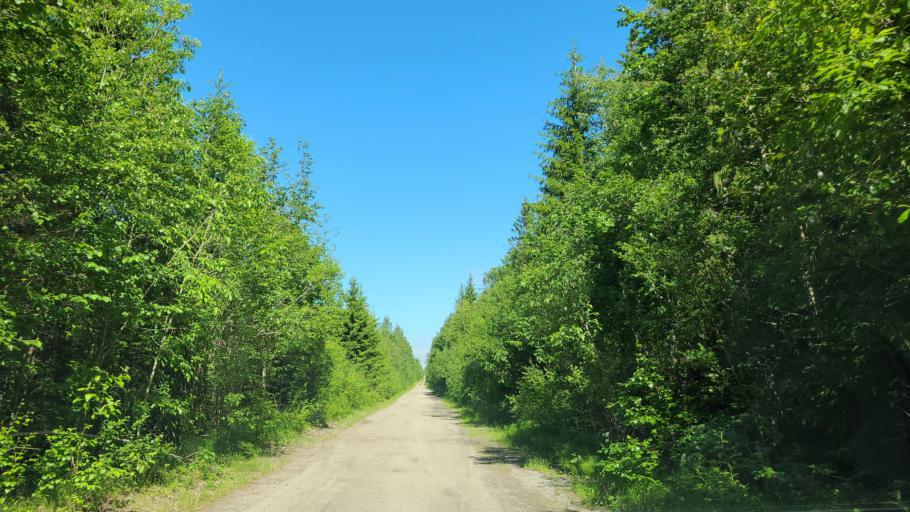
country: SE
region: Vaesternorrland
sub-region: OErnskoeldsviks Kommun
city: Husum
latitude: 63.4219
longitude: 19.2239
